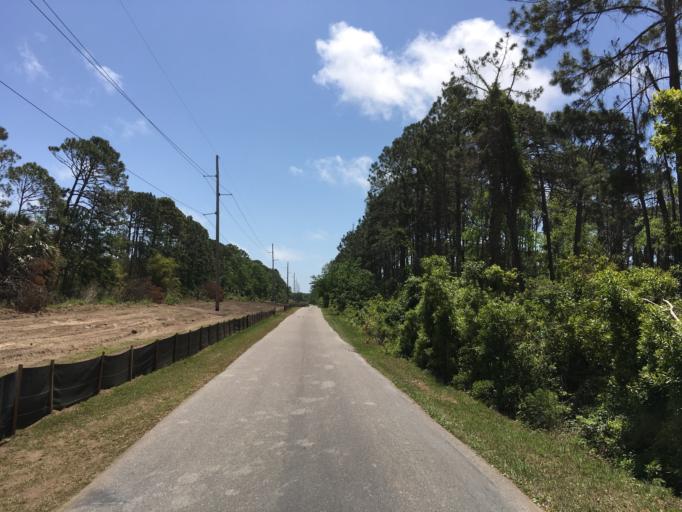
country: US
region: South Carolina
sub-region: Beaufort County
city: Hilton Head Island
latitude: 32.1659
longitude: -80.7669
